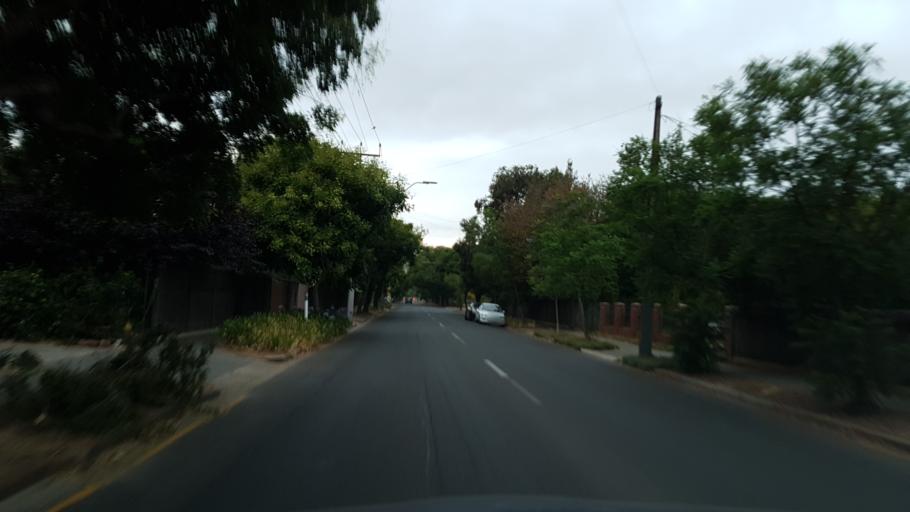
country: AU
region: South Australia
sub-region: Mitcham
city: Hawthorn
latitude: -34.9765
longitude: 138.6028
